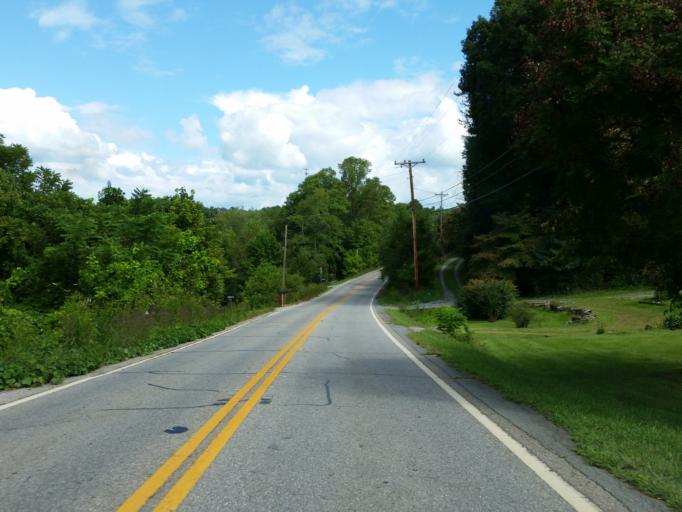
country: US
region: Georgia
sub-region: Fannin County
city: Blue Ridge
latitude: 34.8849
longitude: -84.2577
